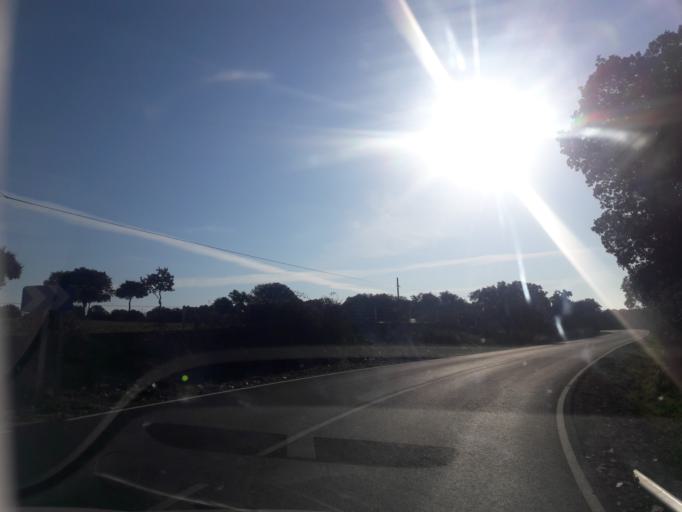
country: ES
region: Castille and Leon
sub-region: Provincia de Salamanca
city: Aldeavieja de Tormes
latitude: 40.5778
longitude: -5.6402
